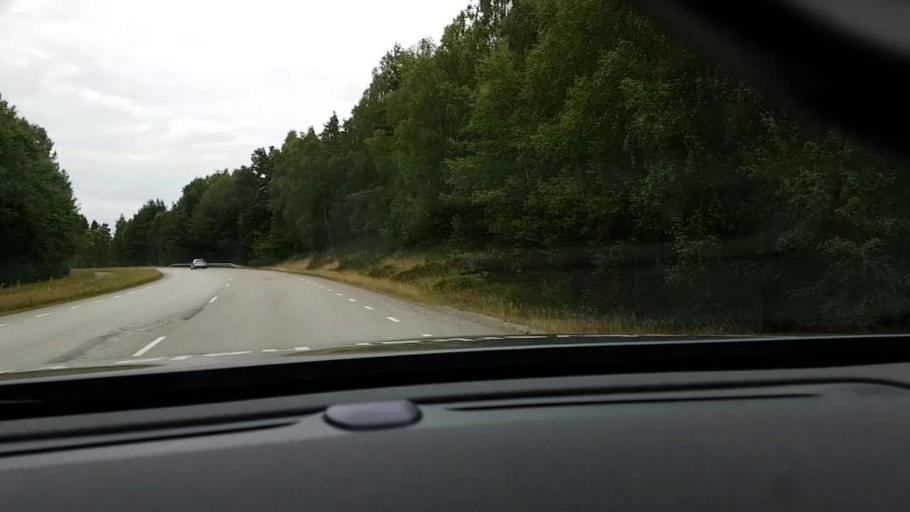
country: SE
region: Skane
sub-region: Hassleholms Kommun
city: Hassleholm
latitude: 56.1637
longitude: 13.8049
